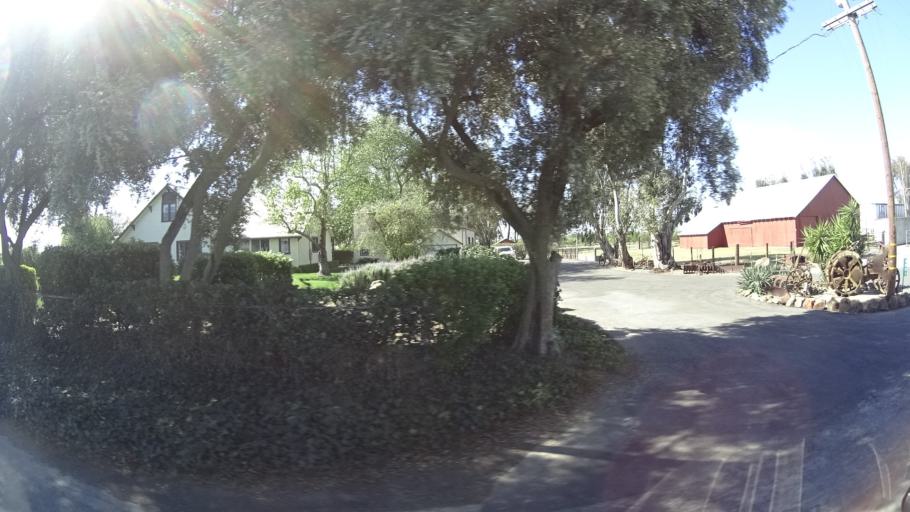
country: US
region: California
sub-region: Glenn County
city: Willows
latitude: 39.6112
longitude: -122.1511
